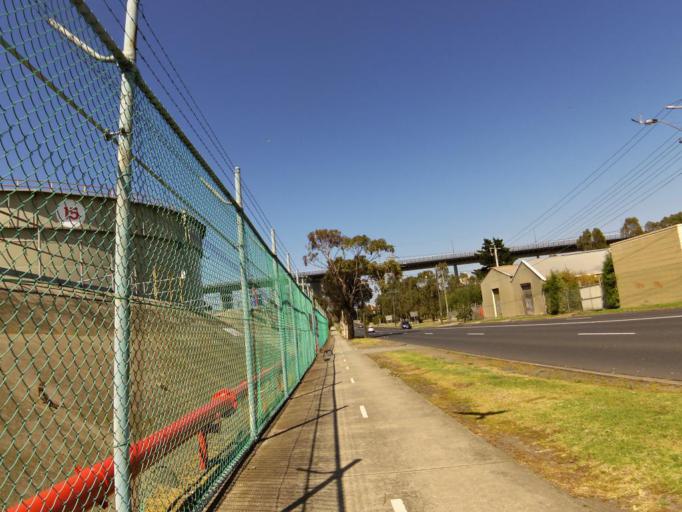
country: AU
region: Victoria
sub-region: Maribyrnong
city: Yarraville
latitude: -37.8235
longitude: 144.8957
